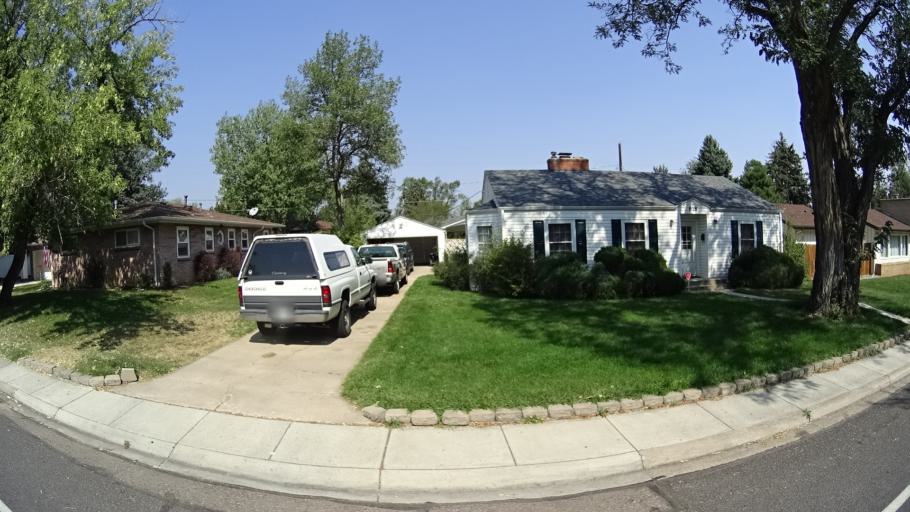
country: US
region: Colorado
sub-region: El Paso County
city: Colorado Springs
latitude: 38.8026
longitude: -104.8385
